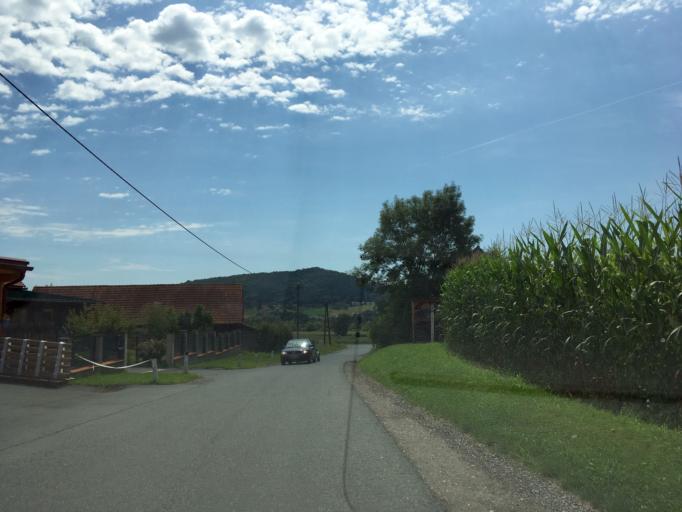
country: AT
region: Styria
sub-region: Politischer Bezirk Leibnitz
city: Gleinstatten
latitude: 46.7643
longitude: 15.3950
